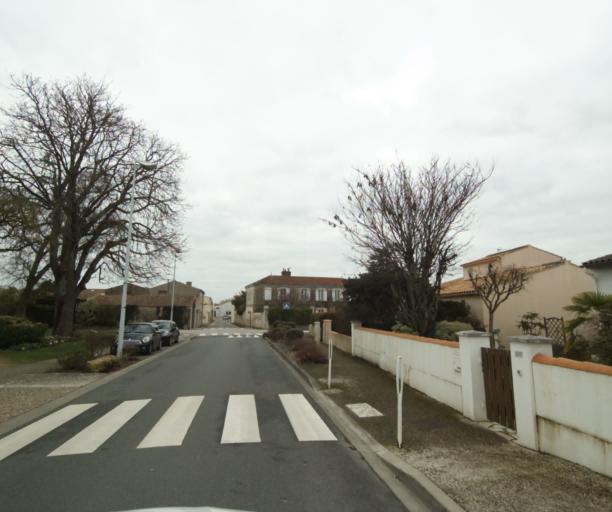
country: FR
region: Poitou-Charentes
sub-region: Departement de la Charente-Maritime
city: Lagord
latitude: 46.1910
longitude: -1.1553
